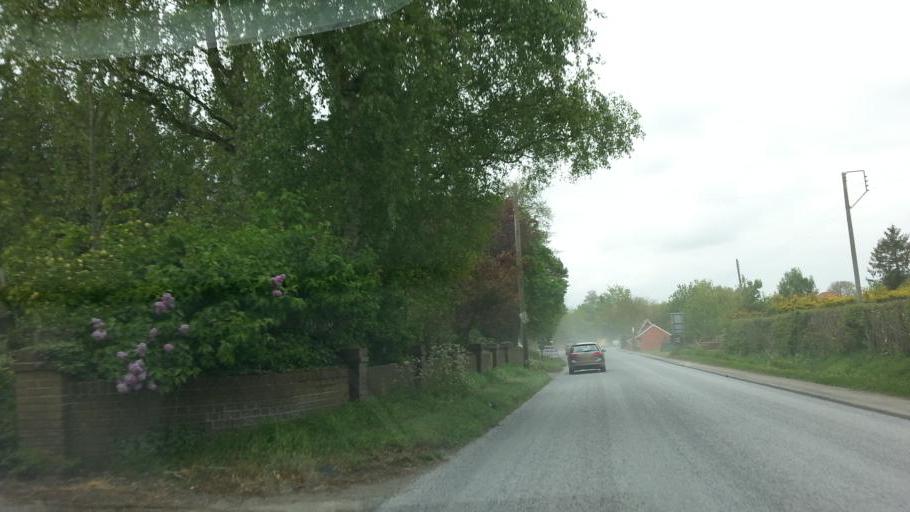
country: GB
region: England
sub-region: Suffolk
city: Bury St Edmunds
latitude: 52.2012
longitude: 0.7590
